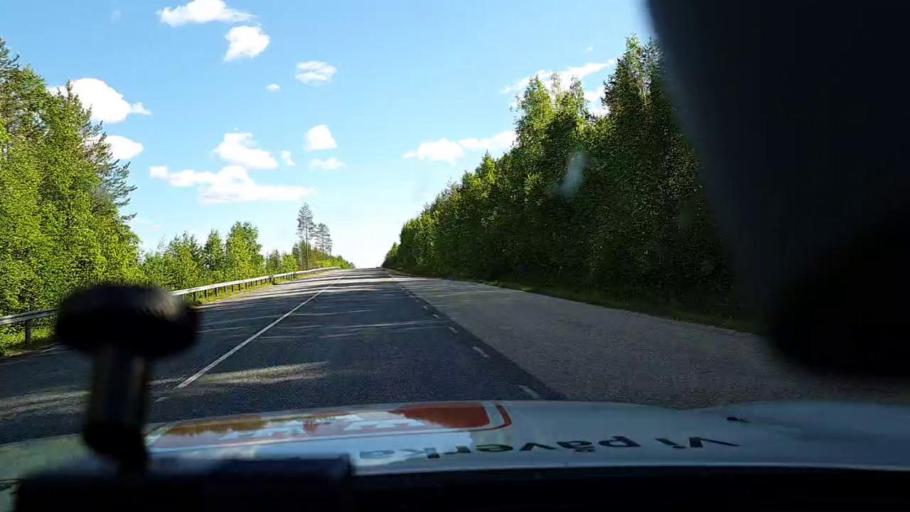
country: SE
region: Norrbotten
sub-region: Overtornea Kommun
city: OEvertornea
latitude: 66.3534
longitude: 23.6476
